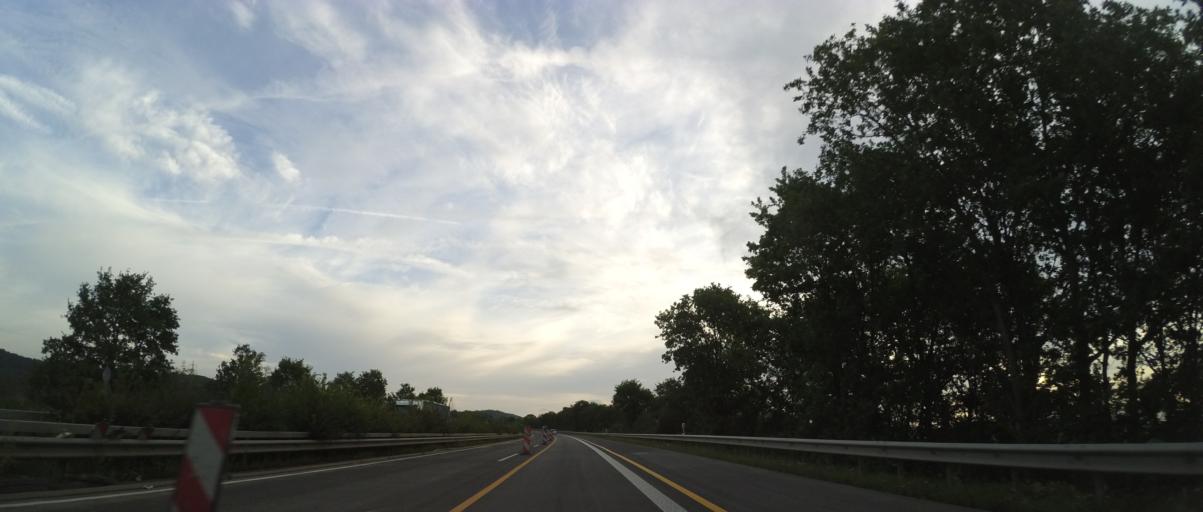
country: DE
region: Rheinland-Pfalz
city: Neuerburg
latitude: 49.9880
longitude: 6.9226
